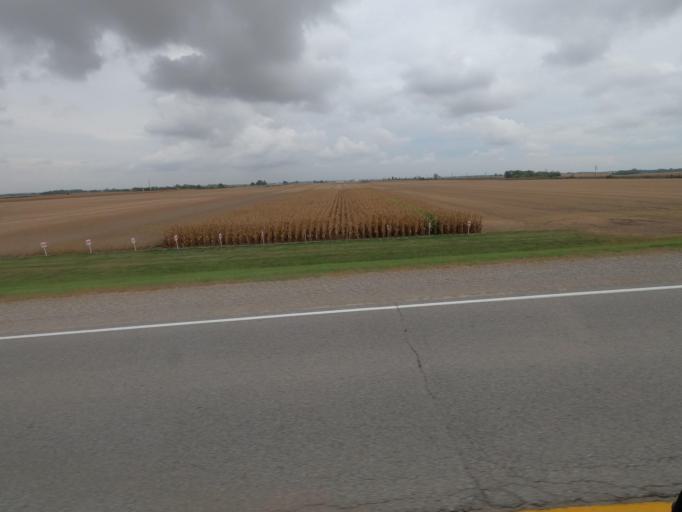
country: US
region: Iowa
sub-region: Wapello County
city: Ottumwa
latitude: 40.9928
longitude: -92.2368
